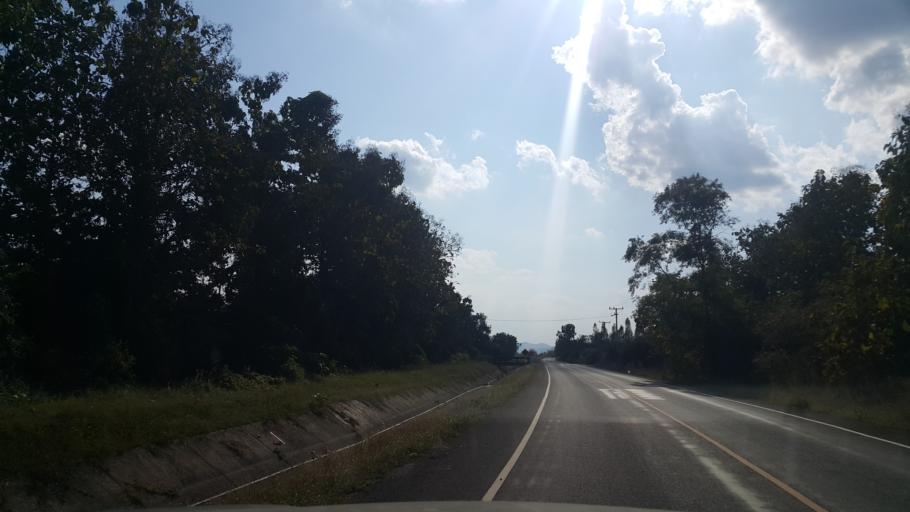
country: TH
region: Lamphun
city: Mae Tha
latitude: 18.5439
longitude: 99.1005
